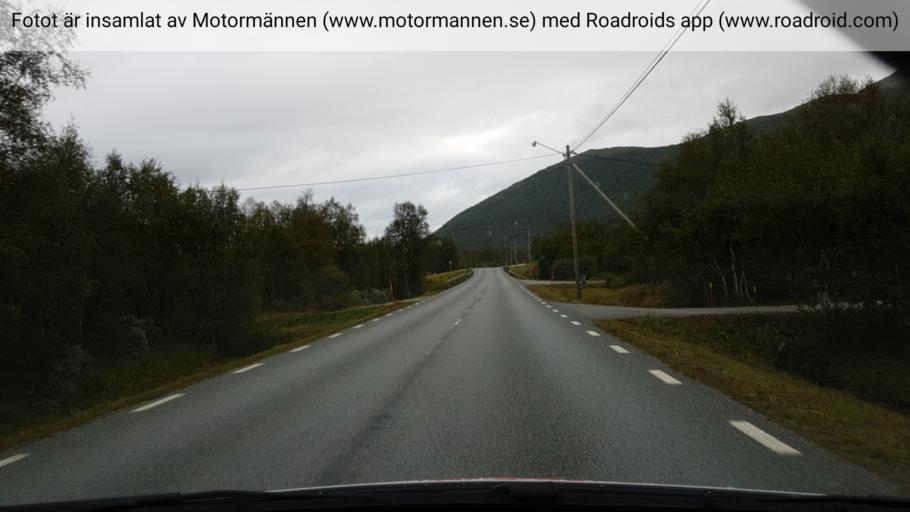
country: NO
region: Nordland
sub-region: Rana
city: Mo i Rana
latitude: 65.9423
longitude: 15.0315
